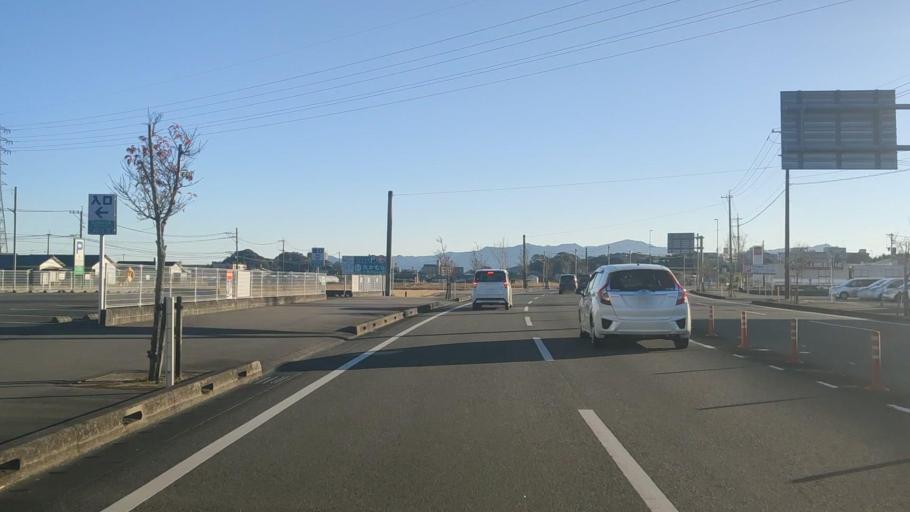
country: JP
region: Miyazaki
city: Miyazaki-shi
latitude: 31.8950
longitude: 131.4070
